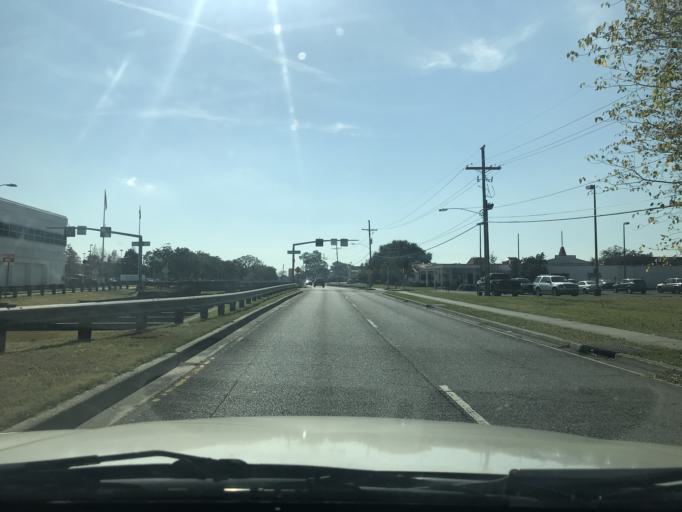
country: US
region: Louisiana
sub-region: Jefferson Parish
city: Marrero
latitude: 29.8924
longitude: -90.0961
